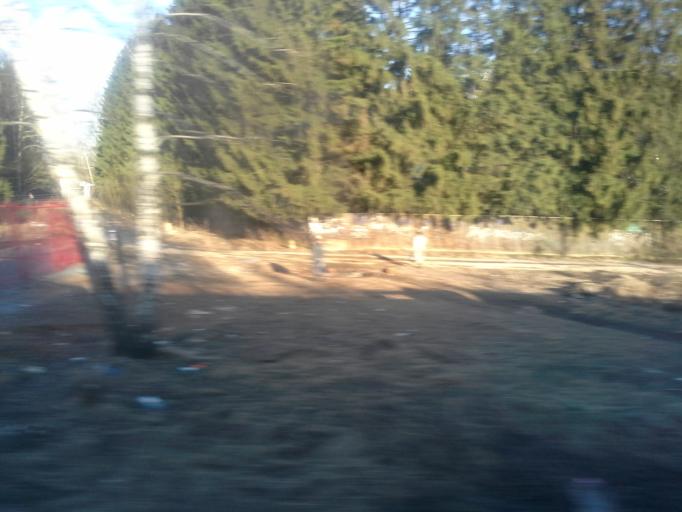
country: RU
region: Moskovskaya
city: Nekrasovskiy
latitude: 56.1234
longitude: 37.5178
